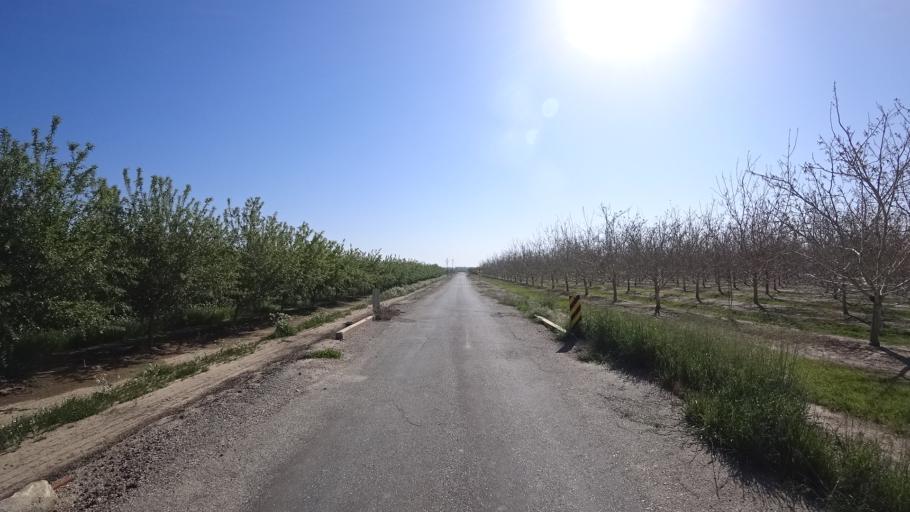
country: US
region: California
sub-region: Glenn County
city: Hamilton City
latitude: 39.6379
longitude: -122.0206
